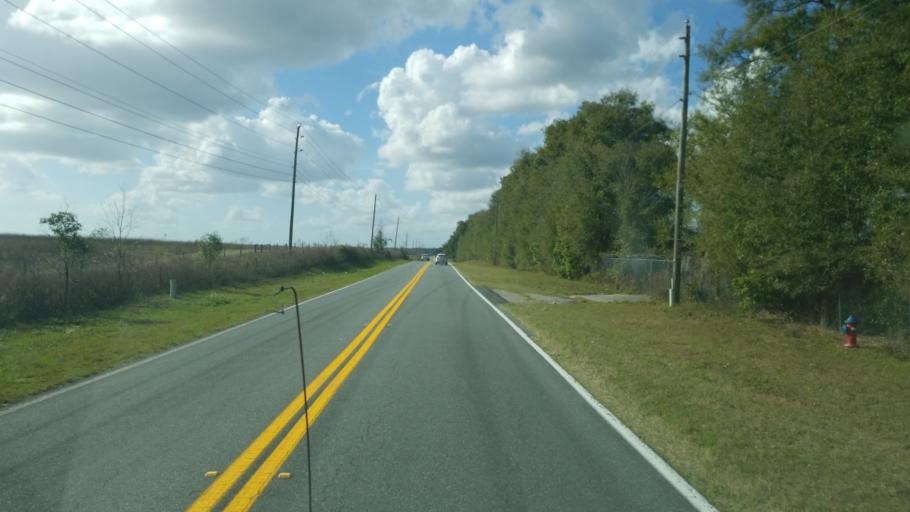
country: US
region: Florida
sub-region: Marion County
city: Ocala
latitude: 29.1502
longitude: -82.2308
